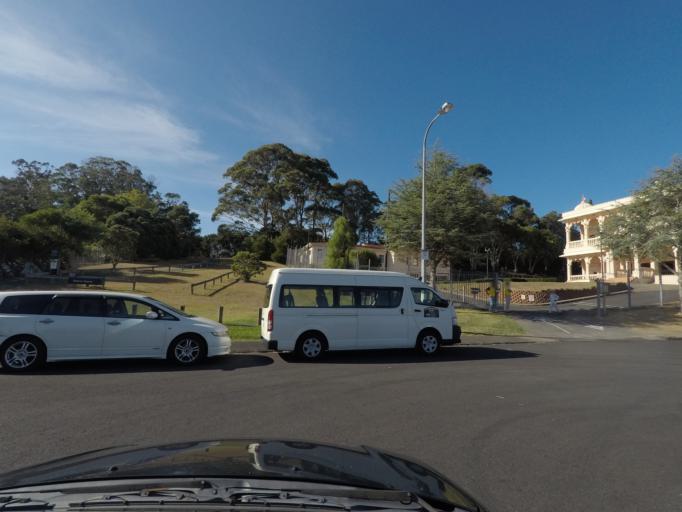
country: NZ
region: Auckland
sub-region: Auckland
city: Rosebank
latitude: -36.9033
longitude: 174.6991
